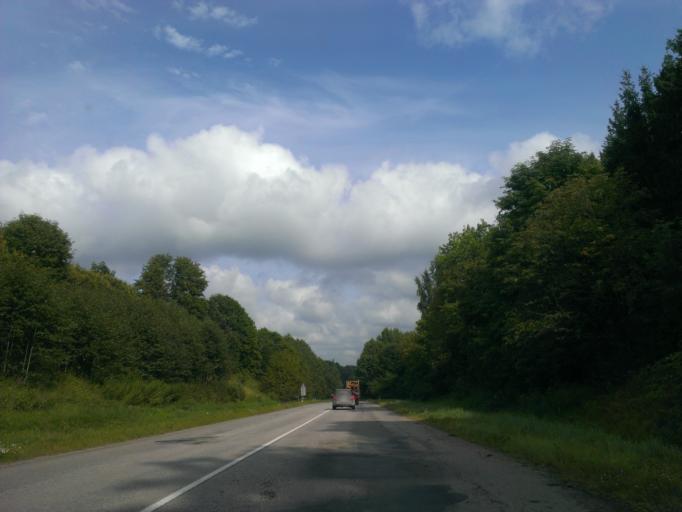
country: LV
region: Priekuli
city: Priekuli
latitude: 57.2554
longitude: 25.3568
